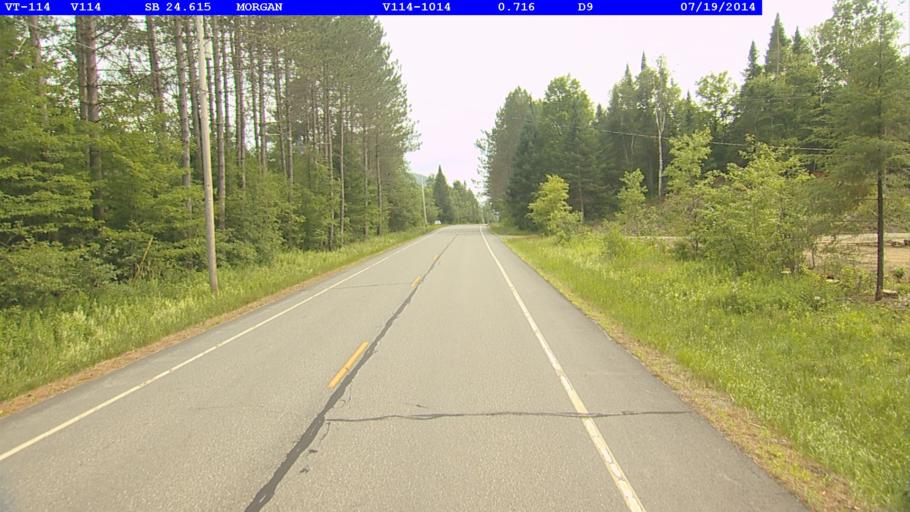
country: CA
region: Quebec
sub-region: Estrie
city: Coaticook
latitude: 44.8569
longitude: -71.9091
